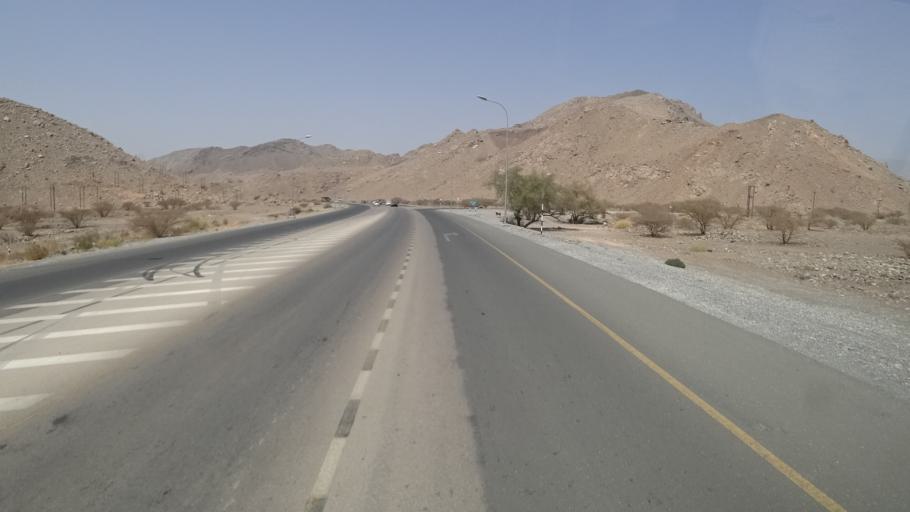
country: OM
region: Muhafazat ad Dakhiliyah
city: Bahla'
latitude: 23.0464
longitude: 57.3124
